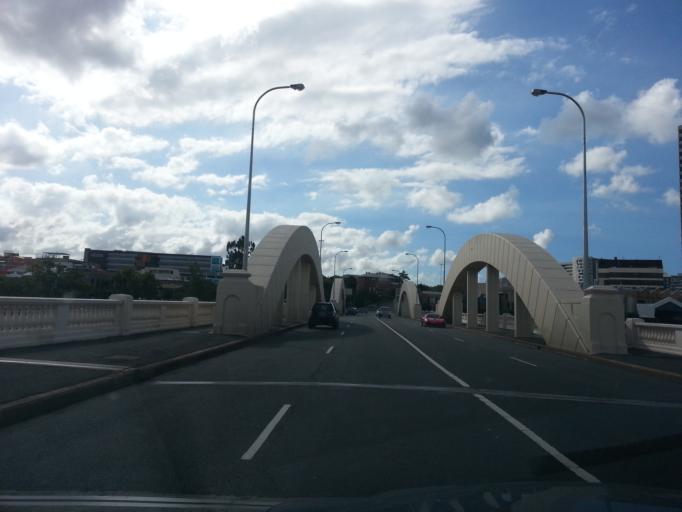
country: AU
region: Queensland
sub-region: Brisbane
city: Spring Hill
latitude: -27.4691
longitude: 153.0155
